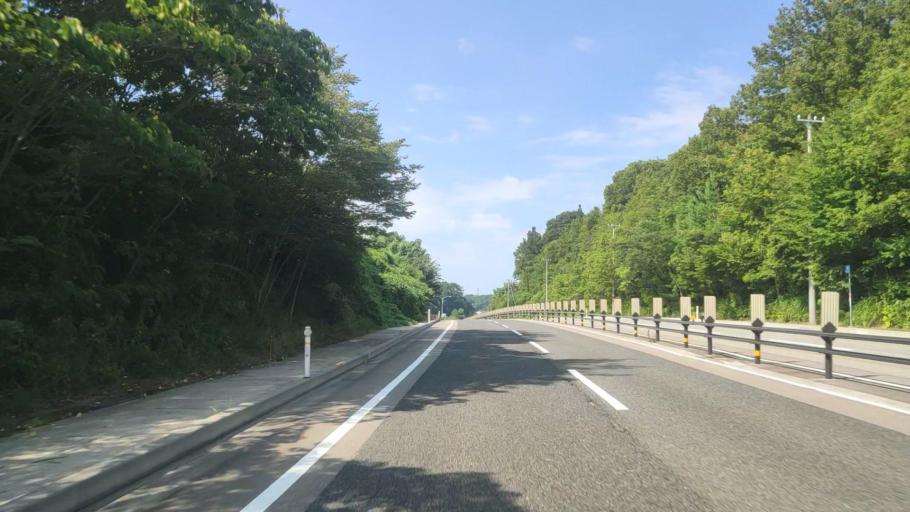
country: JP
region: Ishikawa
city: Komatsu
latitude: 36.4283
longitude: 136.5328
